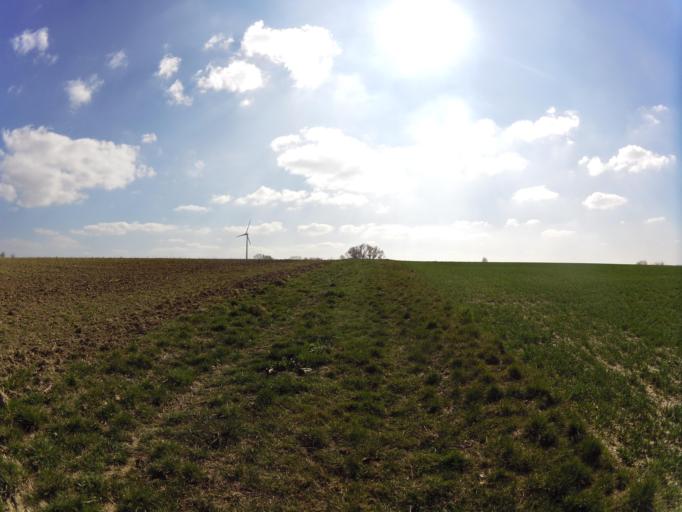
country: DE
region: Bavaria
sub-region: Regierungsbezirk Unterfranken
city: Prosselsheim
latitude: 49.8399
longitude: 10.1534
